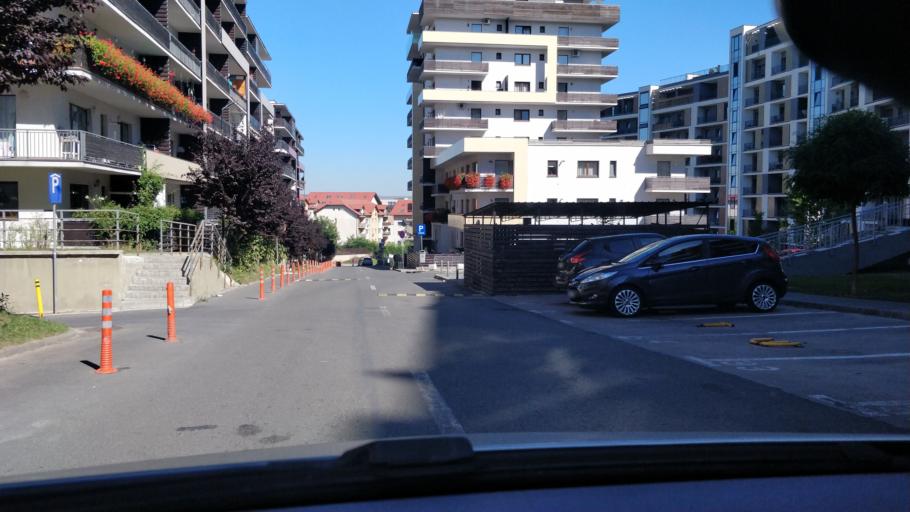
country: RO
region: Cluj
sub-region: Municipiul Cluj-Napoca
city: Cluj-Napoca
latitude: 46.7502
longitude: 23.6000
